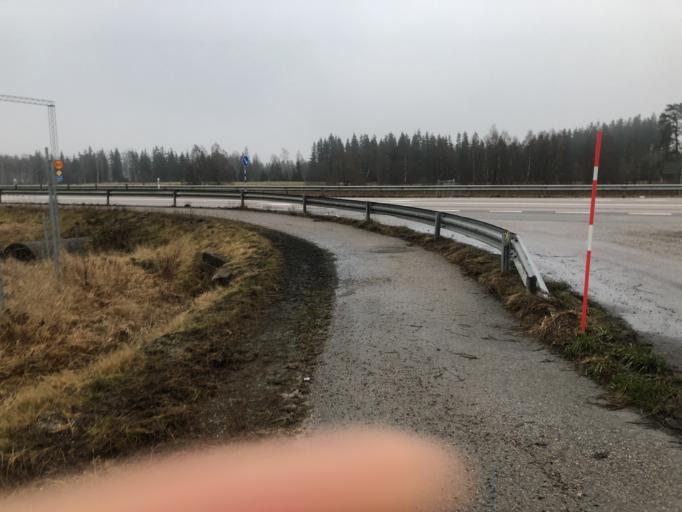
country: SE
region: Vaestra Goetaland
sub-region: Ulricehamns Kommun
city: Ulricehamn
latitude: 57.7971
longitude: 13.5944
